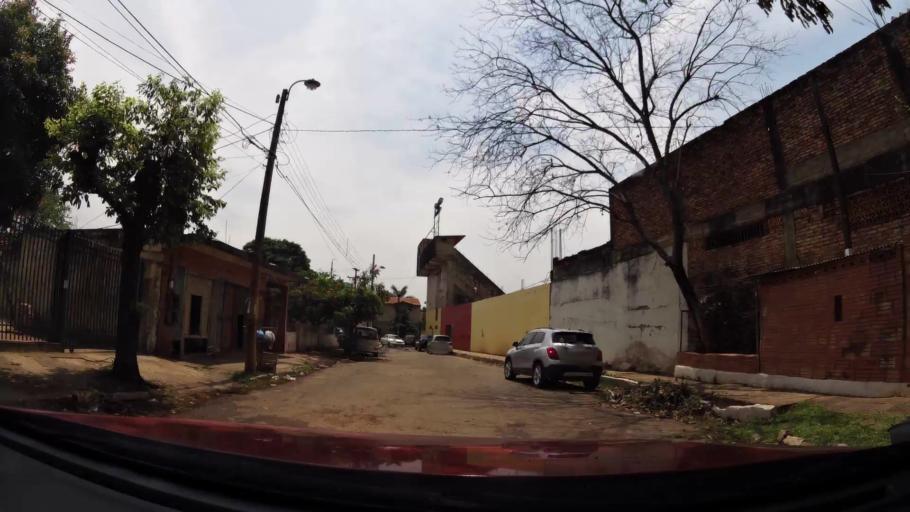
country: PY
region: Central
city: Fernando de la Mora
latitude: -25.3183
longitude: -57.5556
